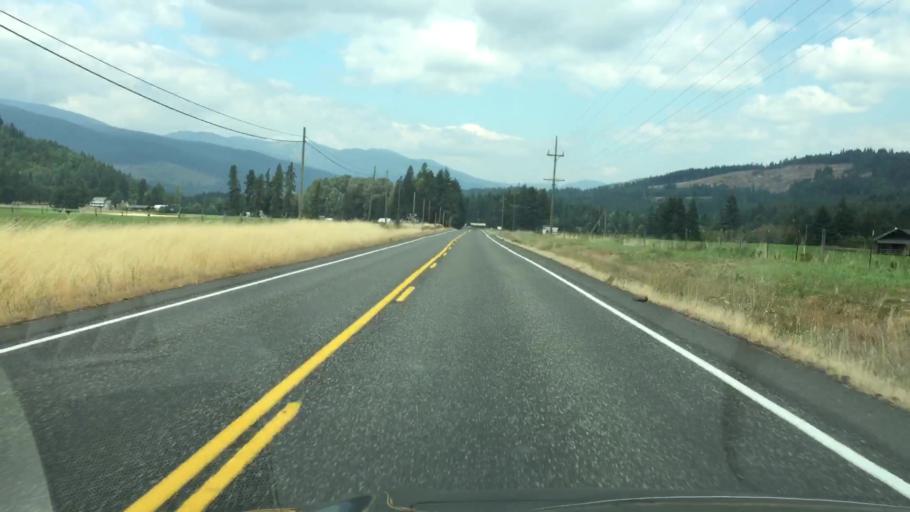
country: US
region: Washington
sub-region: Klickitat County
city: White Salmon
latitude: 45.8216
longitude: -121.4887
